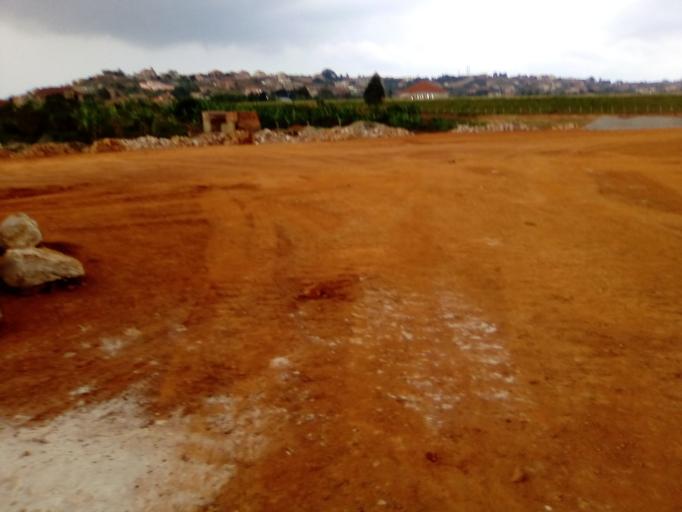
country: UG
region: Central Region
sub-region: Wakiso District
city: Kajansi
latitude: 0.1683
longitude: 32.5127
